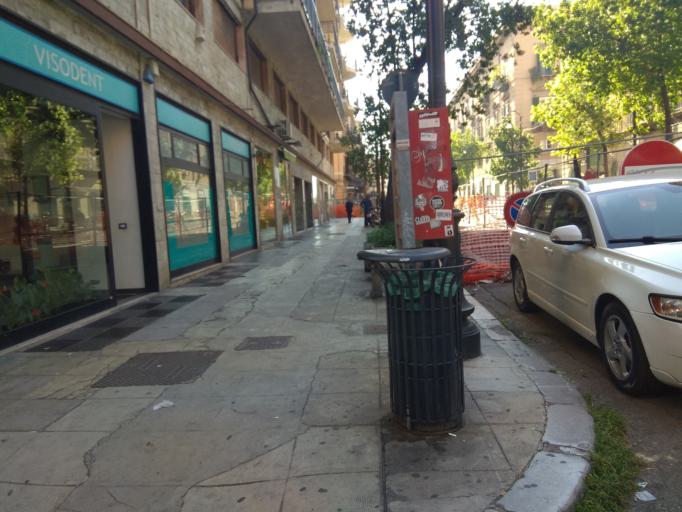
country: IT
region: Sicily
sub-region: Palermo
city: Palermo
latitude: 38.1231
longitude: 13.3601
